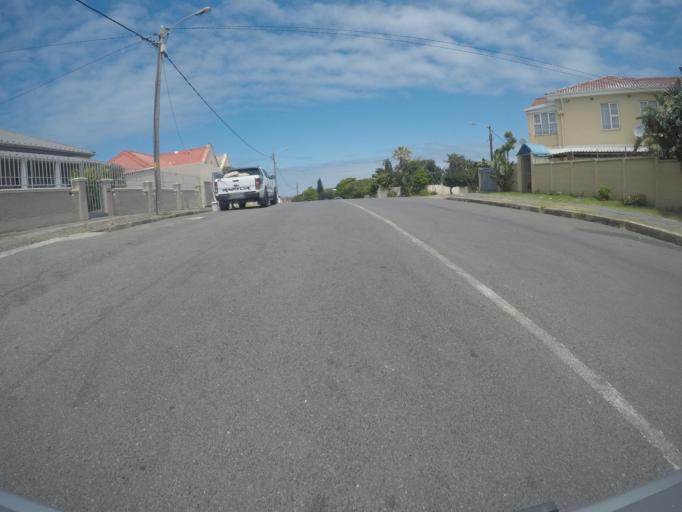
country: ZA
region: Eastern Cape
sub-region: Buffalo City Metropolitan Municipality
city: East London
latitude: -33.0195
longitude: 27.9109
